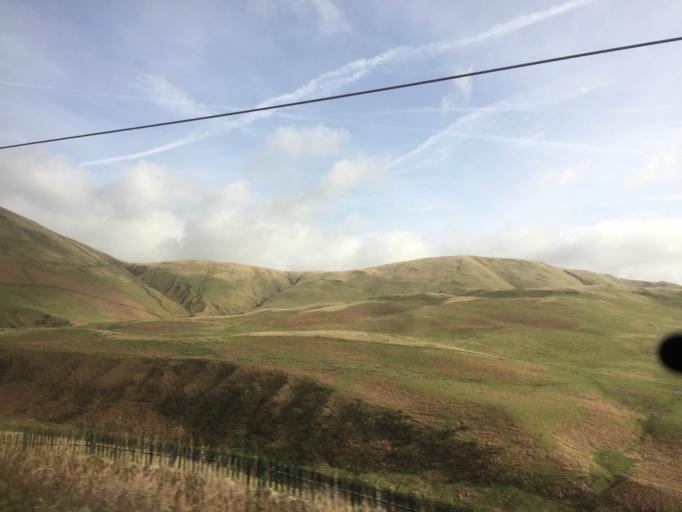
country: GB
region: England
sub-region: Cumbria
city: Sedbergh
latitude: 54.3836
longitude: -2.5815
